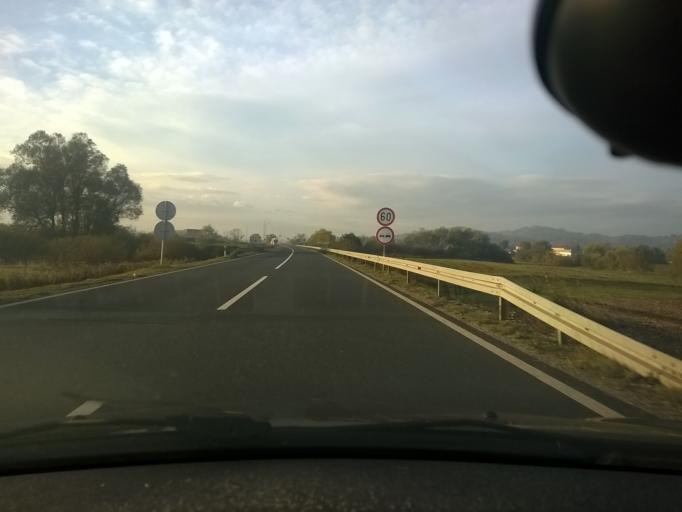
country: HR
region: Zagrebacka
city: Pojatno
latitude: 45.9365
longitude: 15.8204
